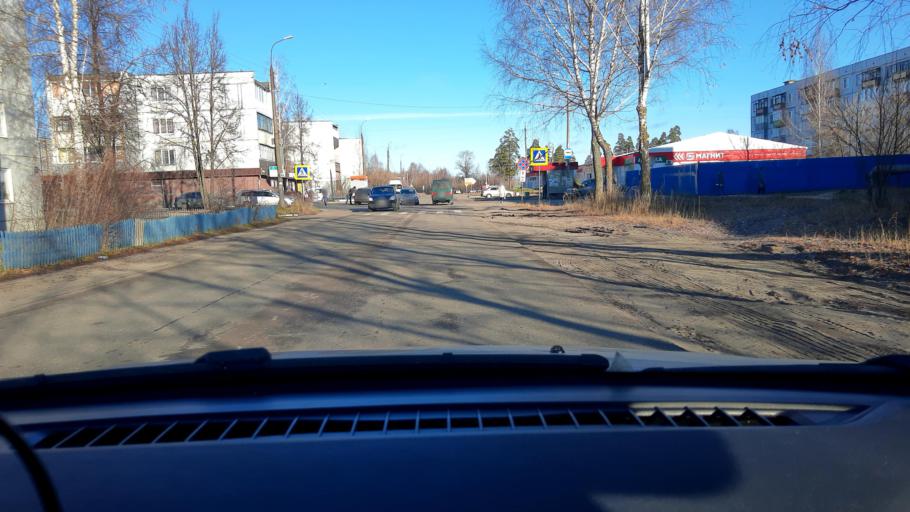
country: RU
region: Nizjnij Novgorod
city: Novosmolinskiy
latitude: 56.2835
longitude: 43.0227
